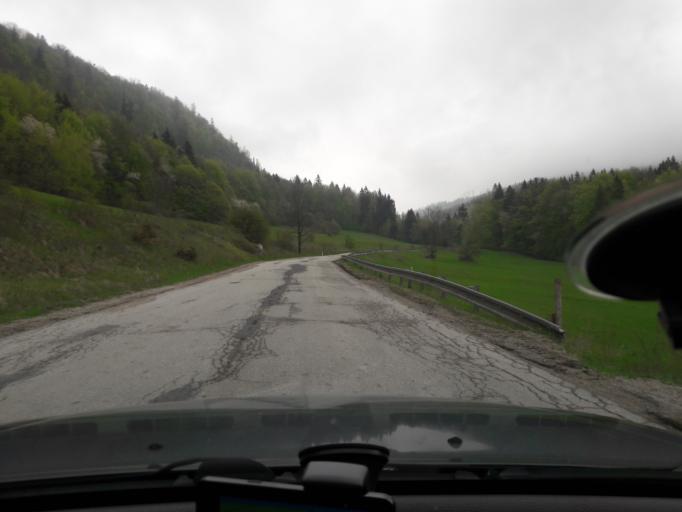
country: SK
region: Banskobystricky
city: Revuca
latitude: 48.7806
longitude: 20.1167
